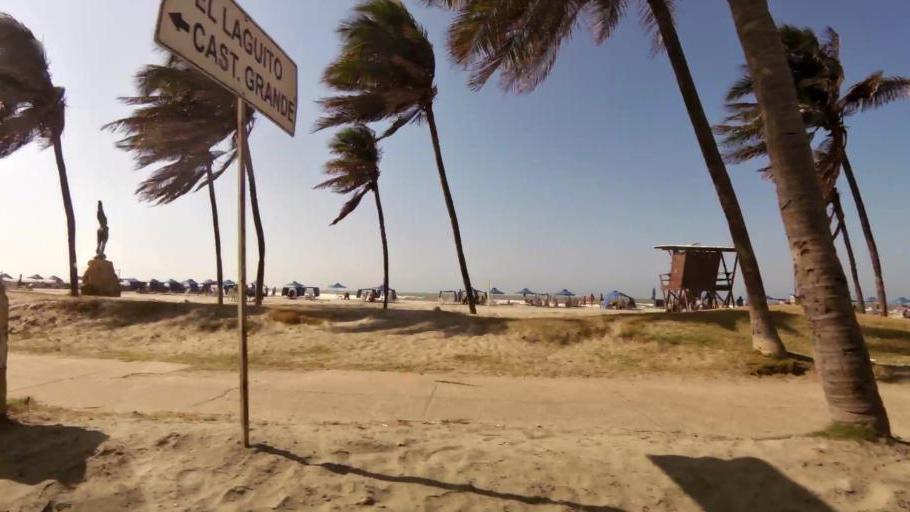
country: CO
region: Bolivar
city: Cartagena
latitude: 10.4020
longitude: -75.5575
